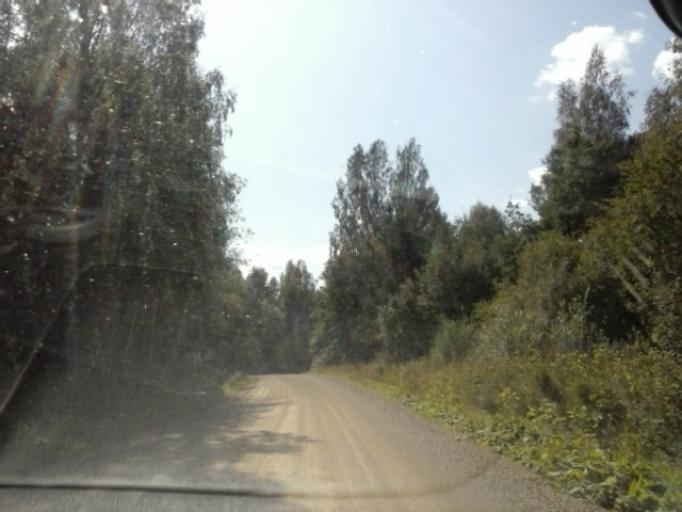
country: EE
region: Polvamaa
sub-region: Polva linn
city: Polva
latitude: 58.1122
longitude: 26.8701
